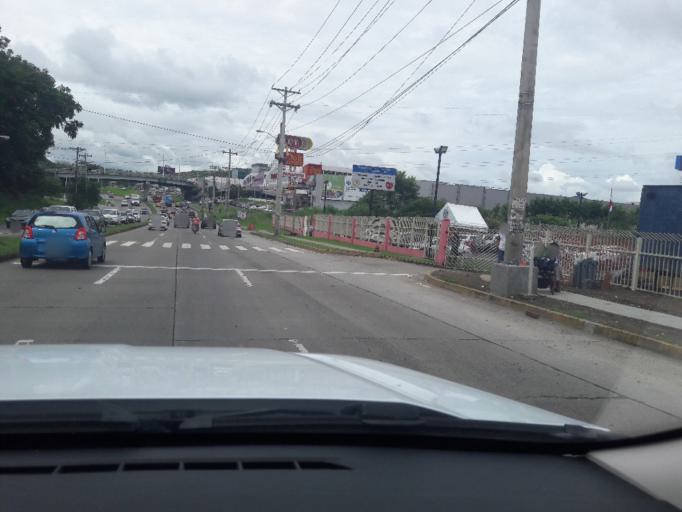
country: PA
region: Panama
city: Panama
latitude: 9.0278
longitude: -79.5302
